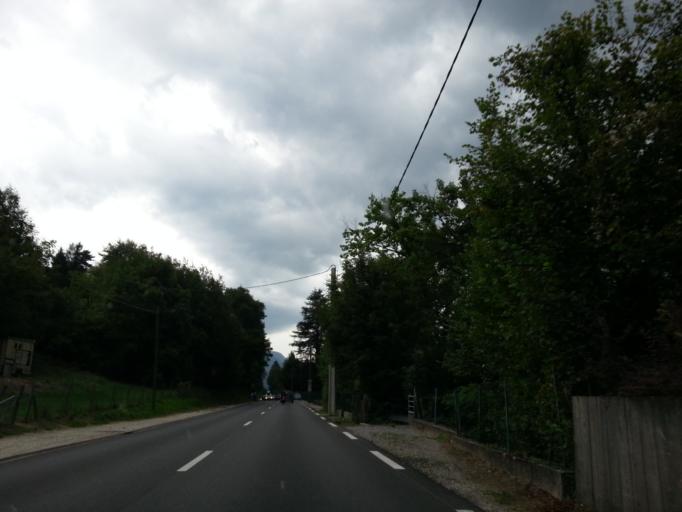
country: FR
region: Rhone-Alpes
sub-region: Departement de la Haute-Savoie
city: Doussard
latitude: 45.8012
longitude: 6.2124
